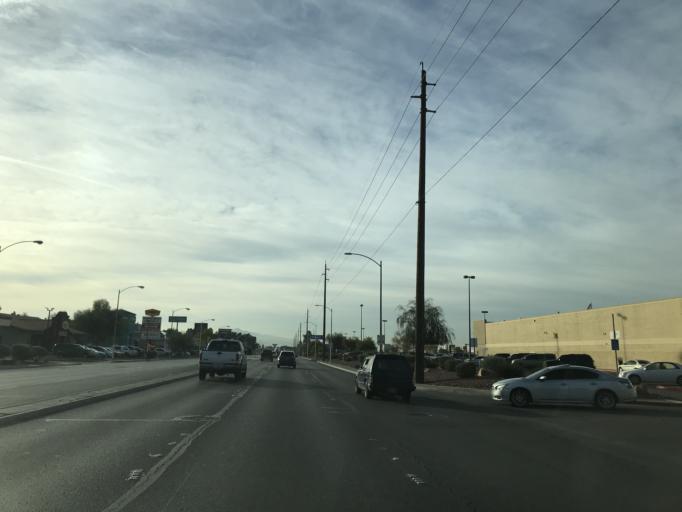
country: US
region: Nevada
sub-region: Clark County
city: Sunrise Manor
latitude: 36.1658
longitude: -115.0622
